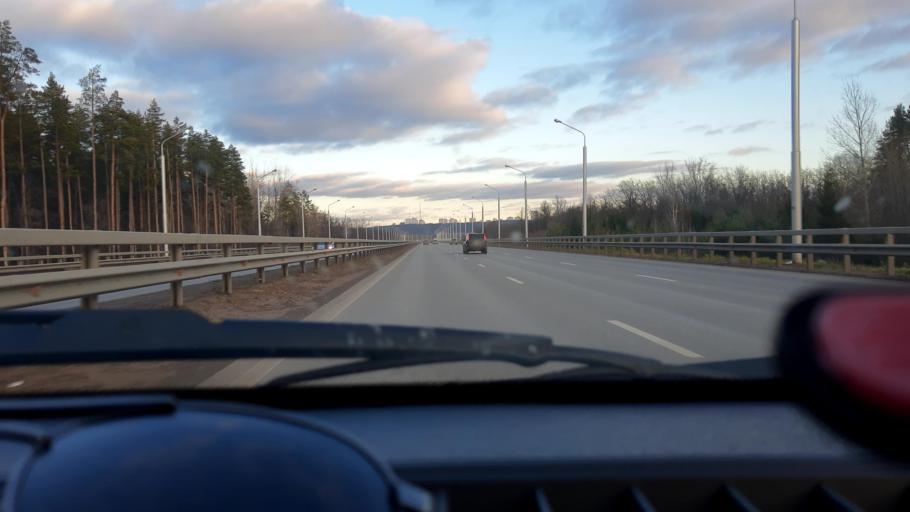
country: RU
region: Bashkortostan
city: Mikhaylovka
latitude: 54.7782
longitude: 55.9295
